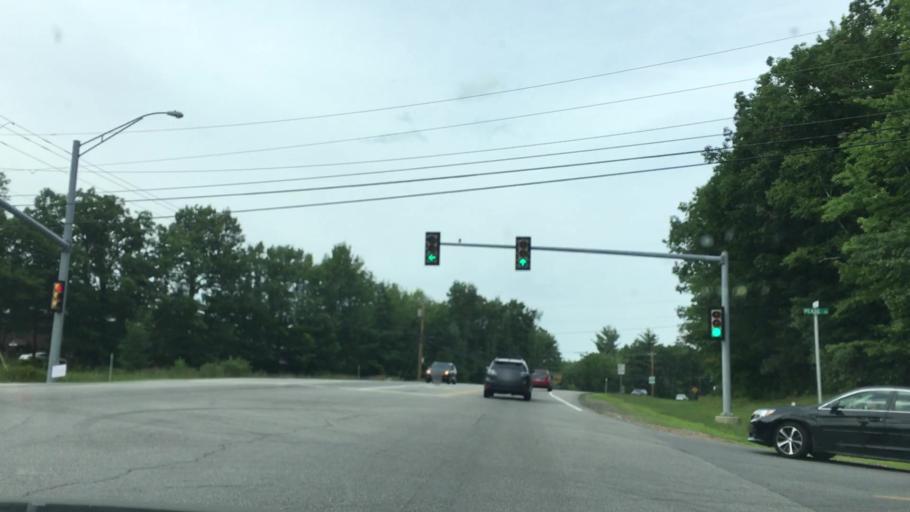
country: US
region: New Hampshire
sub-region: Belknap County
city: Meredith
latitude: 43.6390
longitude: -71.5297
